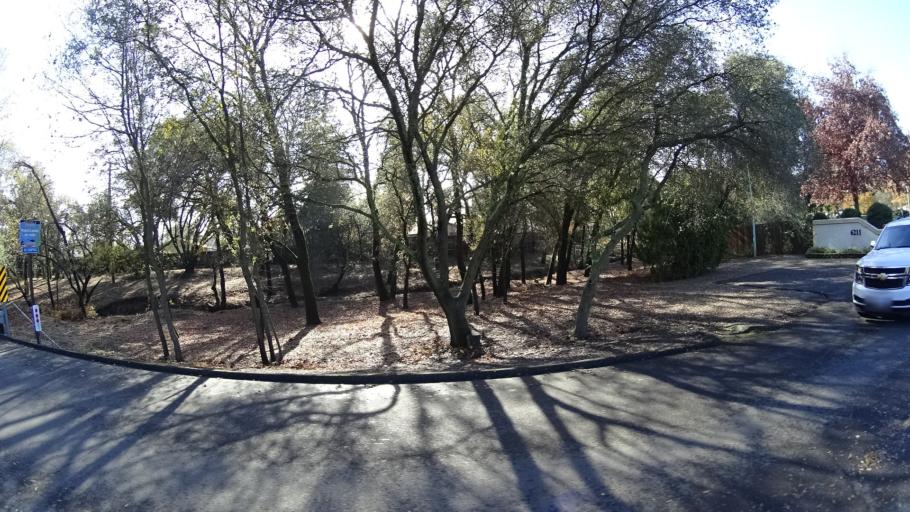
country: US
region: California
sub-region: Sacramento County
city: Antelope
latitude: 38.6887
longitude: -121.3151
